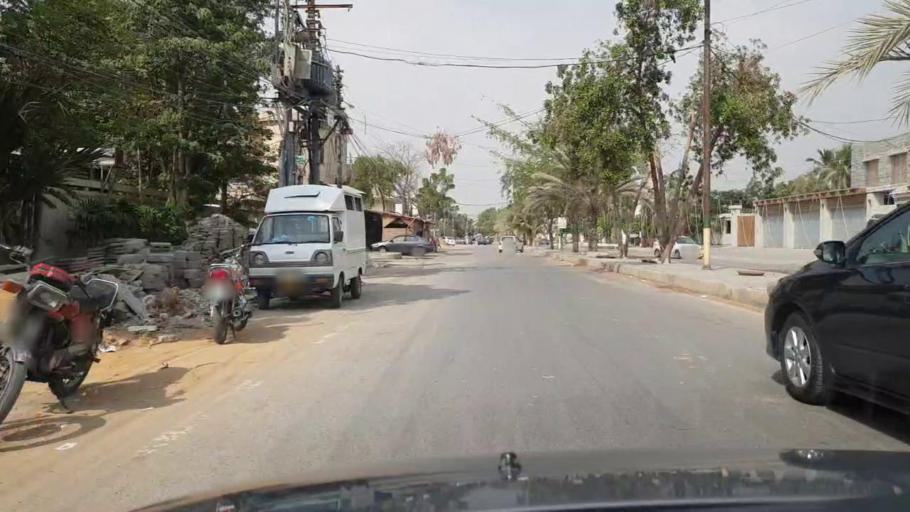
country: PK
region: Sindh
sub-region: Karachi District
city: Karachi
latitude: 24.8731
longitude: 67.0874
